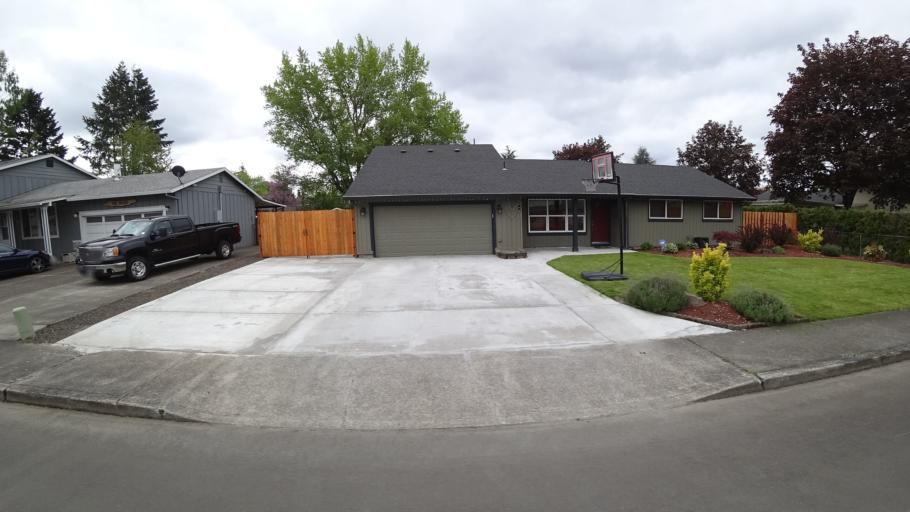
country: US
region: Oregon
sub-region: Washington County
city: Hillsboro
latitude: 45.5373
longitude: -122.9720
